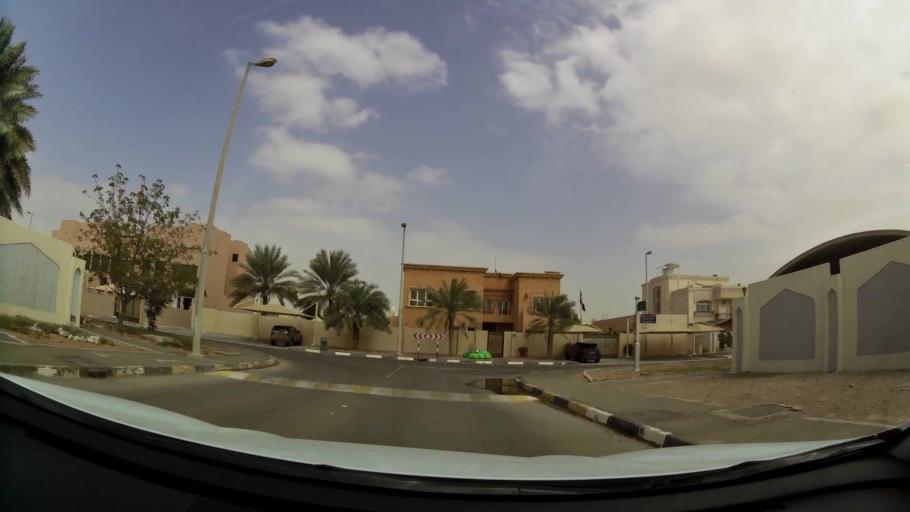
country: AE
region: Abu Dhabi
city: Abu Dhabi
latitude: 24.3936
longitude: 54.5023
